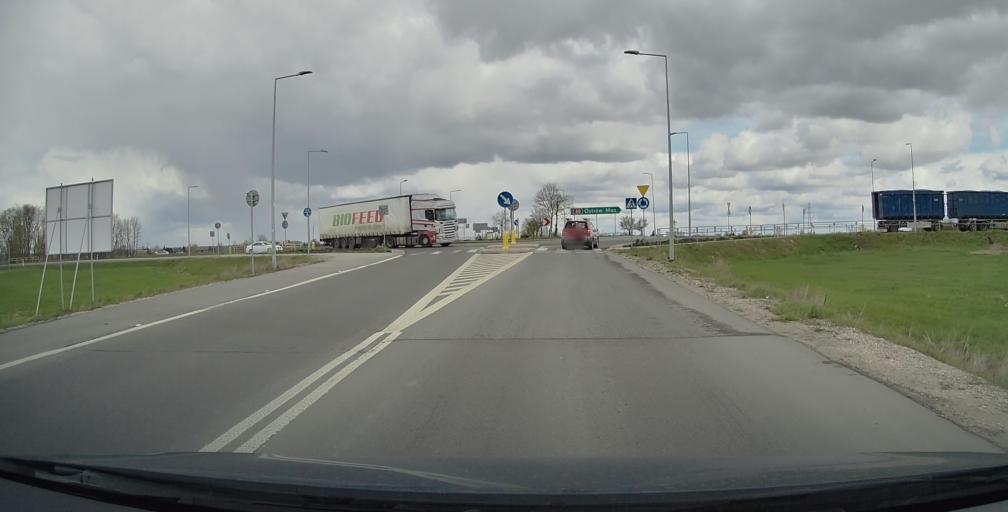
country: PL
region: Masovian Voivodeship
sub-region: Powiat ostrolecki
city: Goworowo
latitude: 52.8669
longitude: 21.5647
